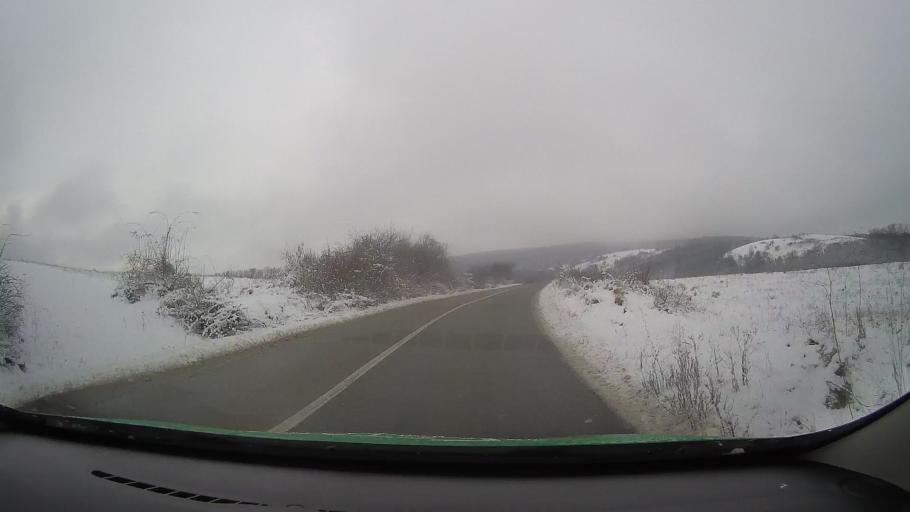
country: RO
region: Hunedoara
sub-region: Oras Hateg
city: Hateg
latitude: 45.6428
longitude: 22.9208
